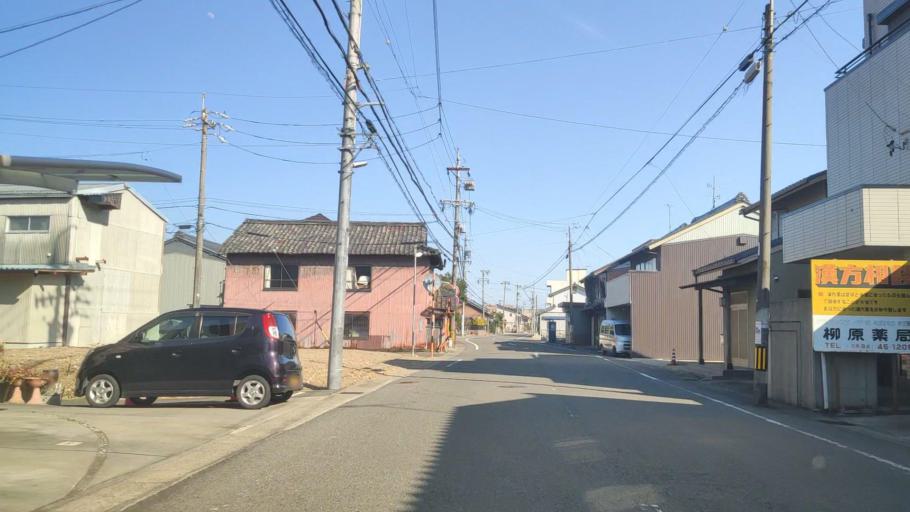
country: JP
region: Gifu
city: Gifu-shi
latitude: 35.4002
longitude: 136.7877
